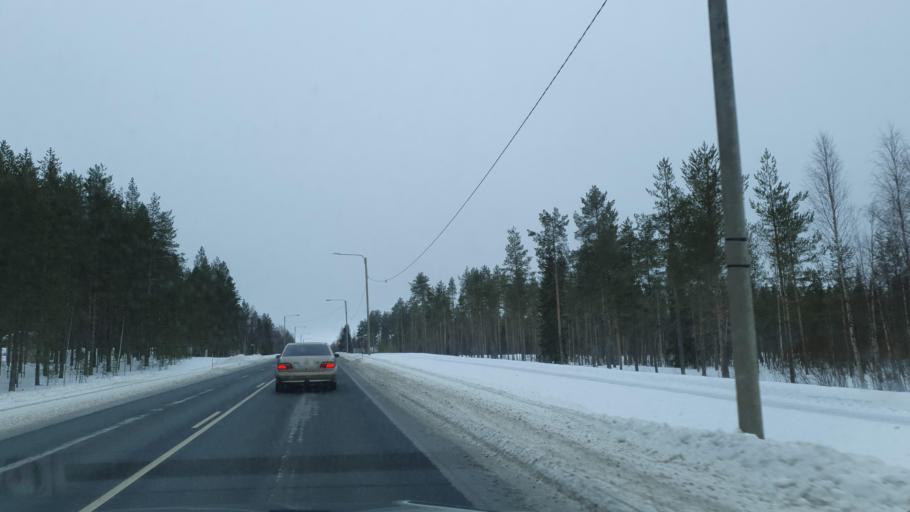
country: FI
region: Lapland
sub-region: Torniolaakso
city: Pello
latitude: 66.7429
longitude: 23.9171
